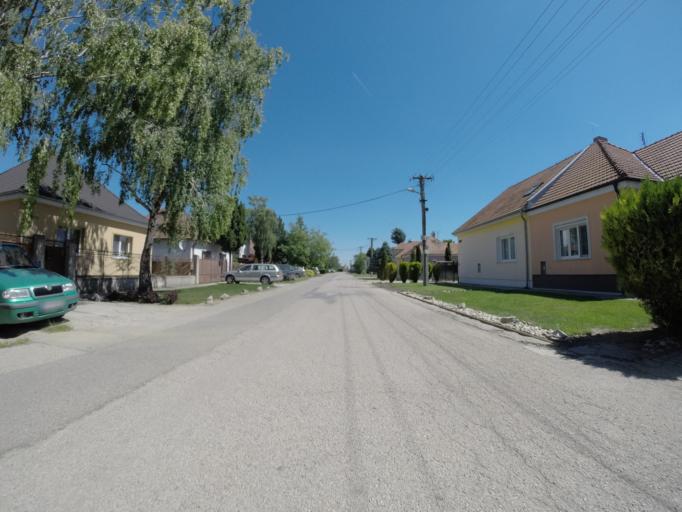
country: SK
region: Trnavsky
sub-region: Okres Galanta
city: Galanta
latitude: 48.2041
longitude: 17.7055
